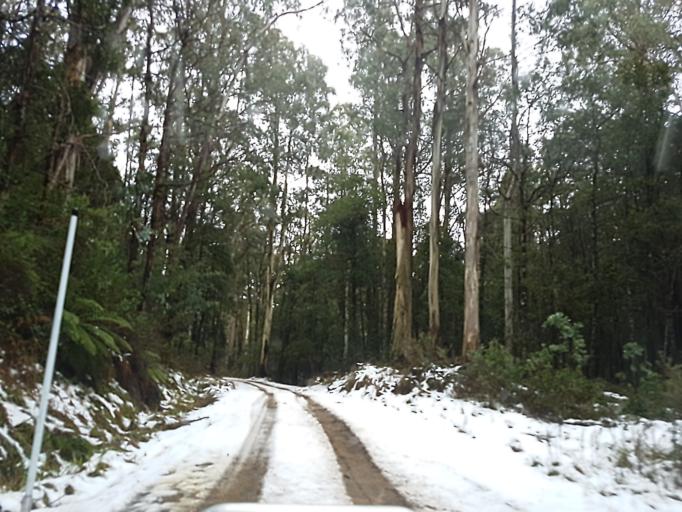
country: AU
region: Victoria
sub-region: Murrindindi
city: Alexandra
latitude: -37.4359
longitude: 145.8964
